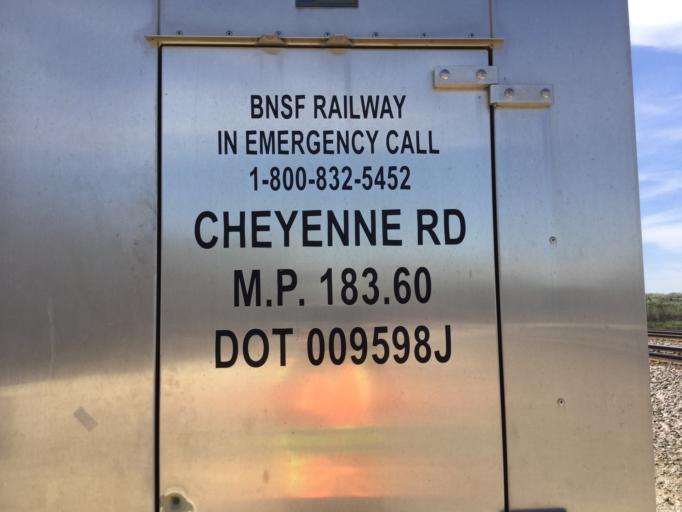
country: US
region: Kansas
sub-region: Butler County
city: Augusta
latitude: 37.6967
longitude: -96.9488
